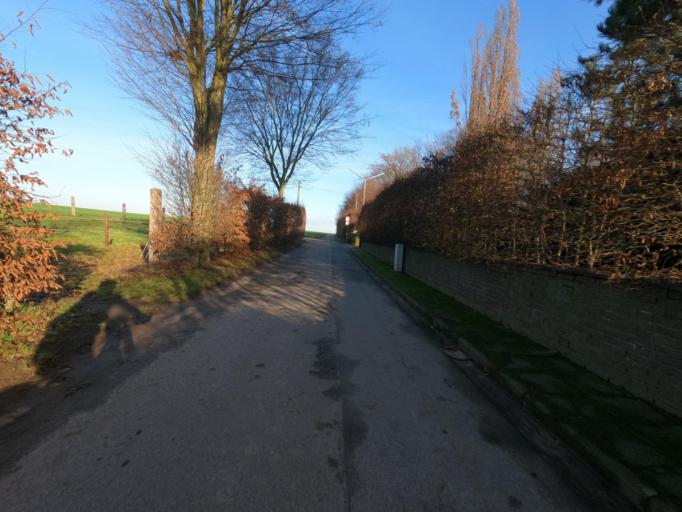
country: DE
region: North Rhine-Westphalia
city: Julich
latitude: 50.9279
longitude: 6.3981
